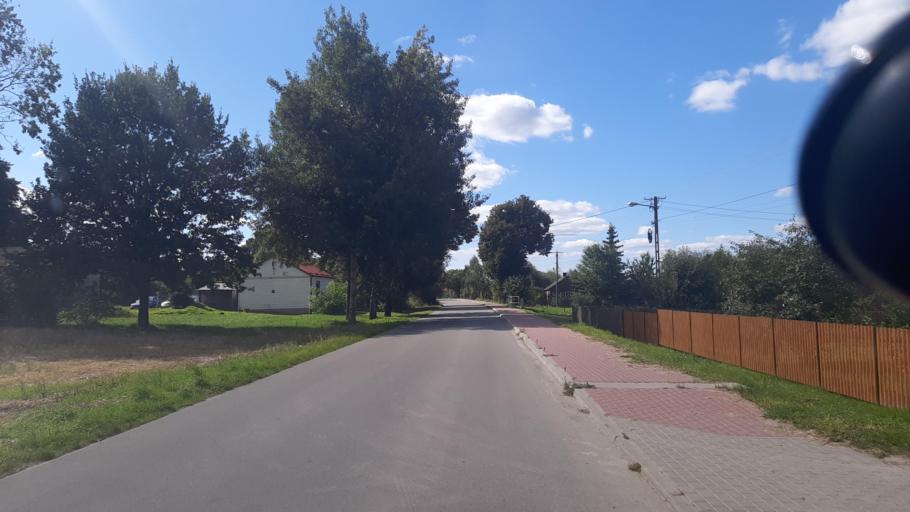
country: PL
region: Lublin Voivodeship
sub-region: Powiat lubelski
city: Garbow
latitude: 51.4030
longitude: 22.3447
